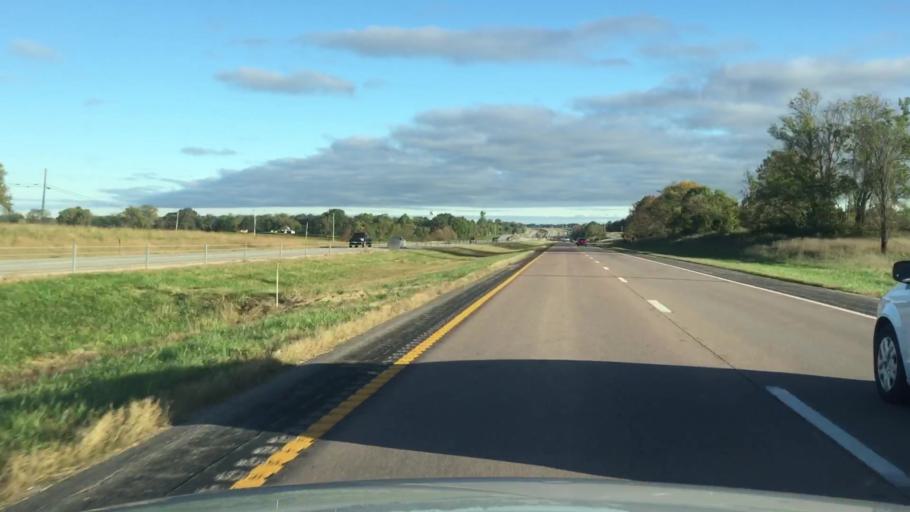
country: US
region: Missouri
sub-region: Boone County
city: Ashland
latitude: 38.8407
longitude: -92.2491
